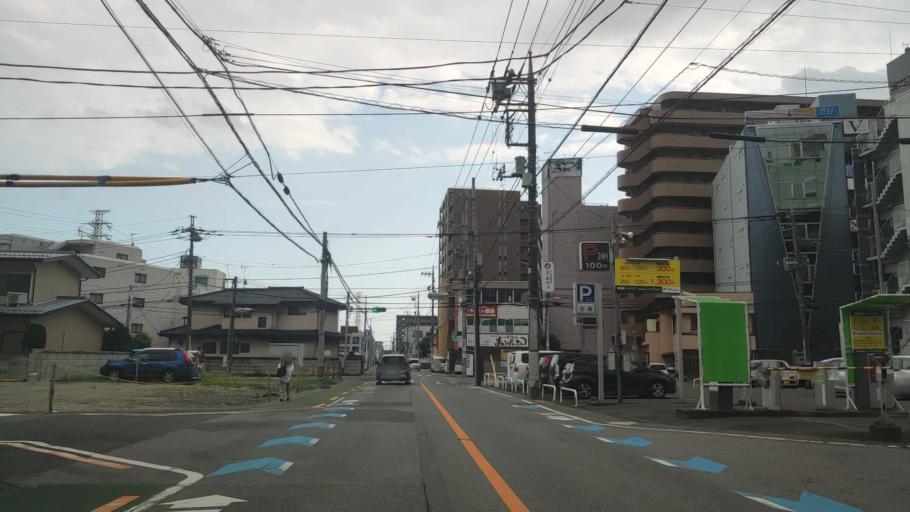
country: JP
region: Tochigi
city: Utsunomiya-shi
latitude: 36.5569
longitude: 139.9017
